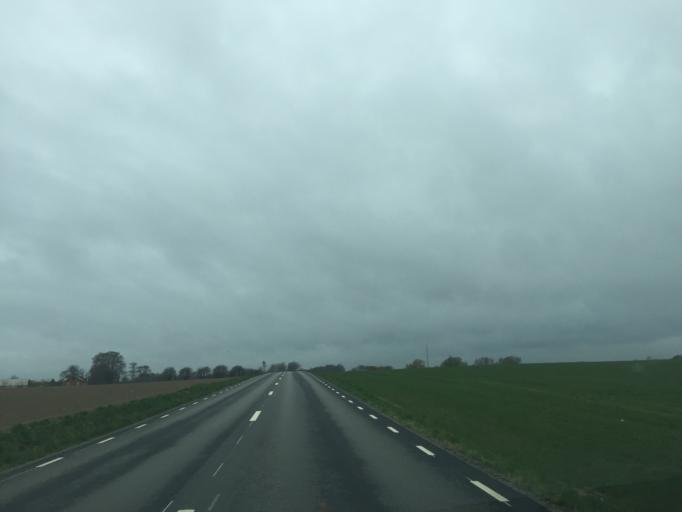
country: SE
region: Skane
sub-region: Skurups Kommun
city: Skivarp
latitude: 55.4244
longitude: 13.5930
